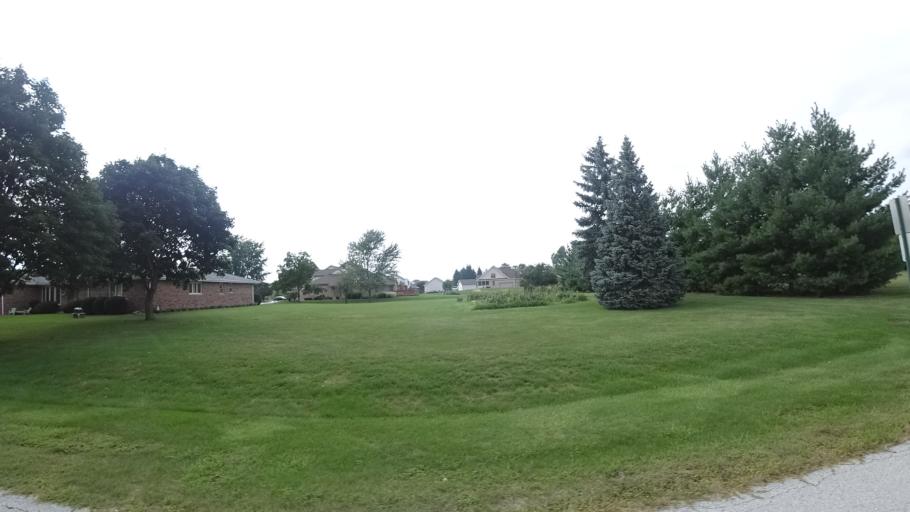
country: US
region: Illinois
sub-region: Cook County
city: Tinley Park
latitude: 41.5568
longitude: -87.7790
